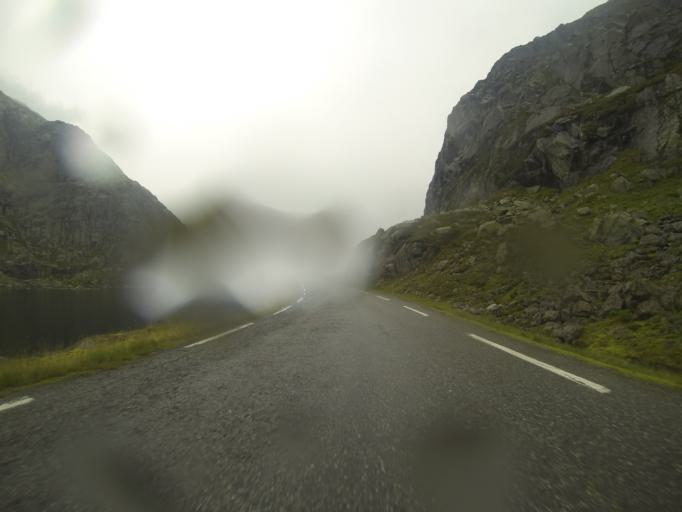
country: NO
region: Hordaland
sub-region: Odda
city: Odda
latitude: 59.7680
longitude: 6.7355
